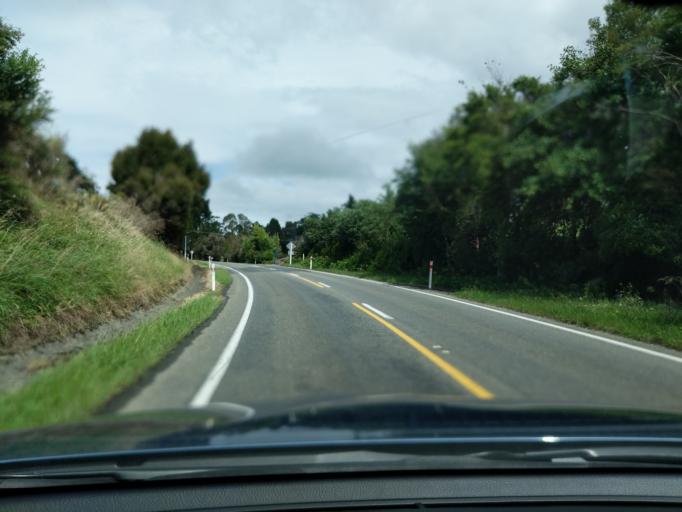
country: NZ
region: Tasman
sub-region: Tasman District
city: Takaka
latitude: -40.6817
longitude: 172.6736
